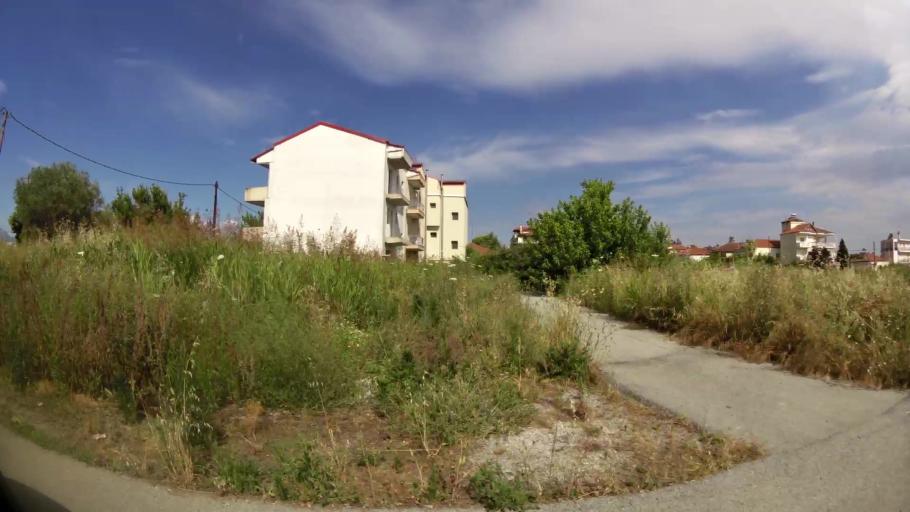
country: GR
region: Central Macedonia
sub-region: Nomos Pierias
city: Katerini
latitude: 40.2776
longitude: 22.5180
